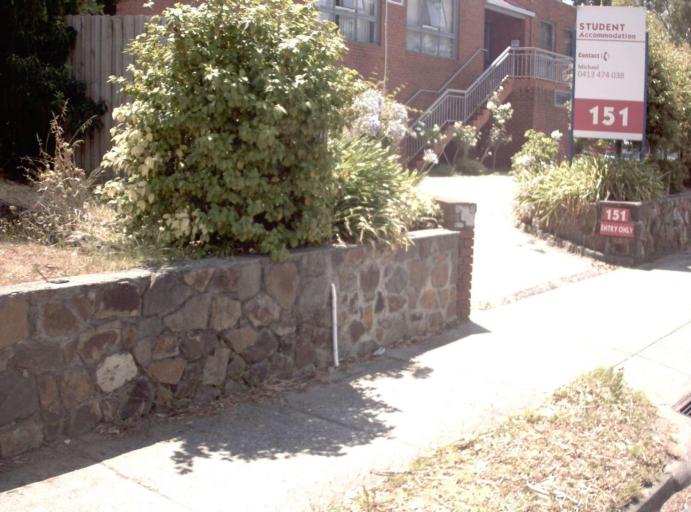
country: AU
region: Victoria
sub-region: Whitehorse
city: Vermont South
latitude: -37.8711
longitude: 145.1674
